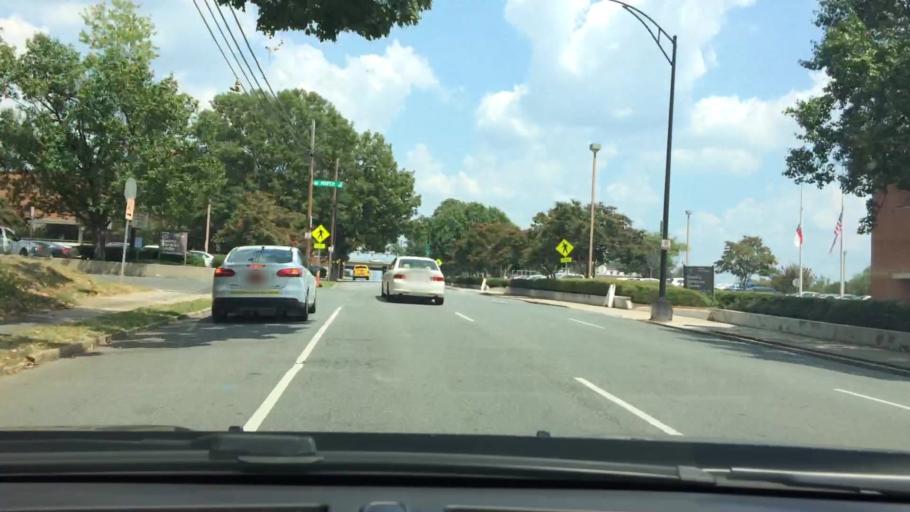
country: US
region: North Carolina
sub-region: Mecklenburg County
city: Charlotte
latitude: 35.2305
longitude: -80.8361
